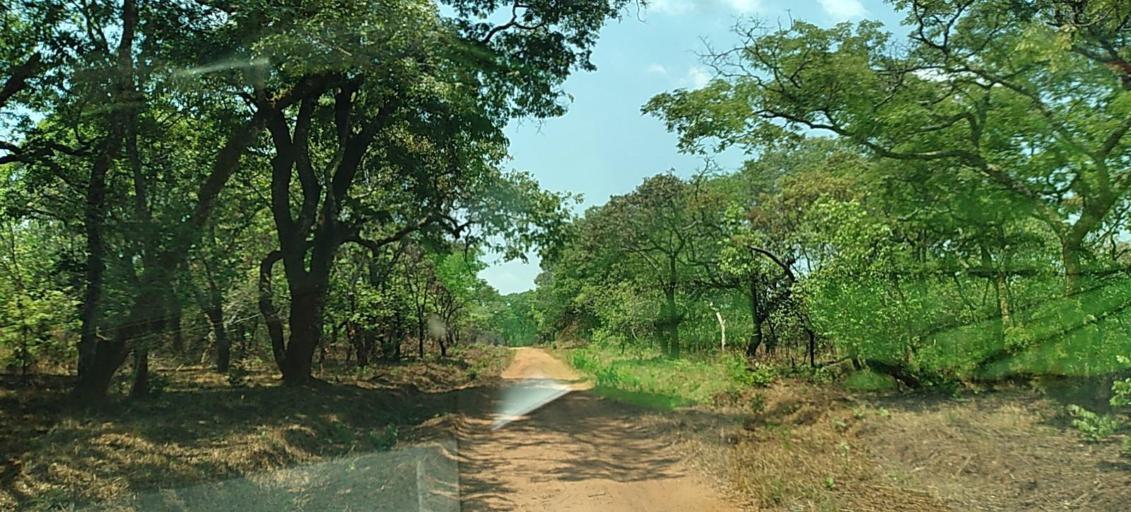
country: CD
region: Katanga
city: Kolwezi
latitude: -11.3573
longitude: 25.2083
